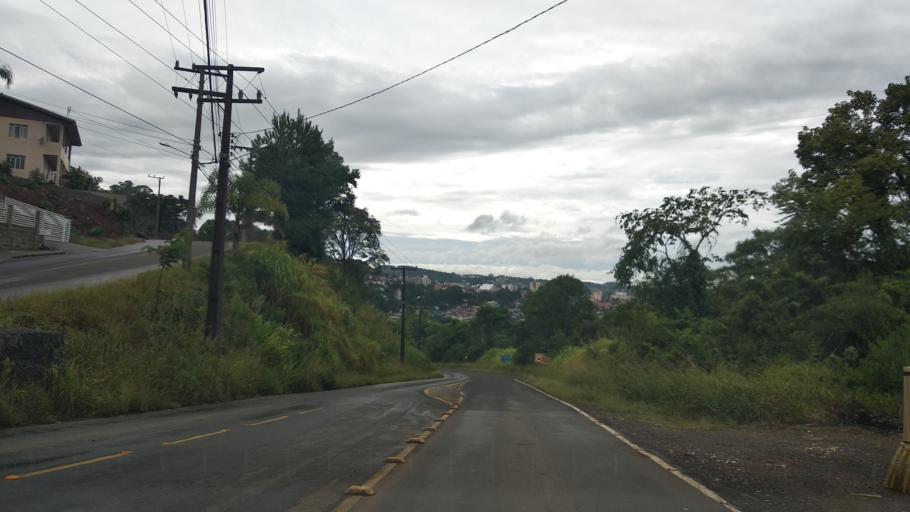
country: BR
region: Santa Catarina
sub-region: Videira
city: Videira
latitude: -27.0010
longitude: -51.1753
